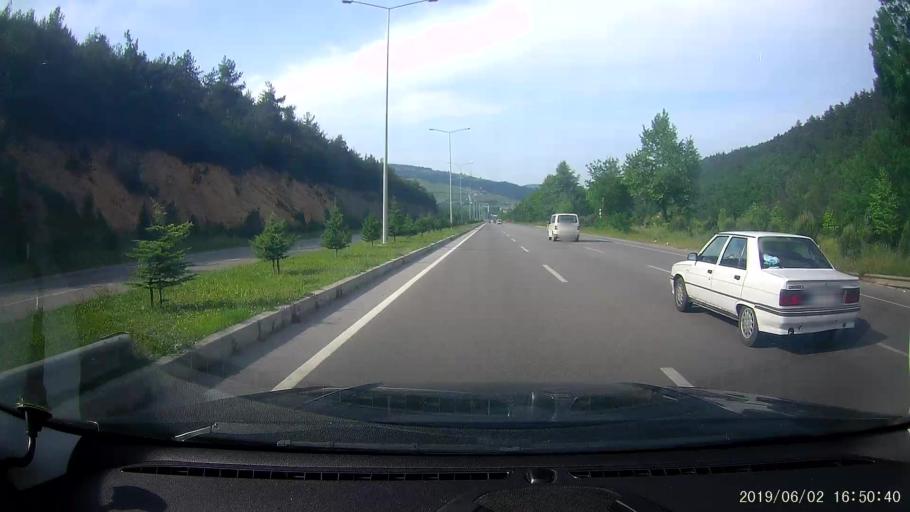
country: TR
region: Samsun
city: Taflan
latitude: 41.2595
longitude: 36.1746
